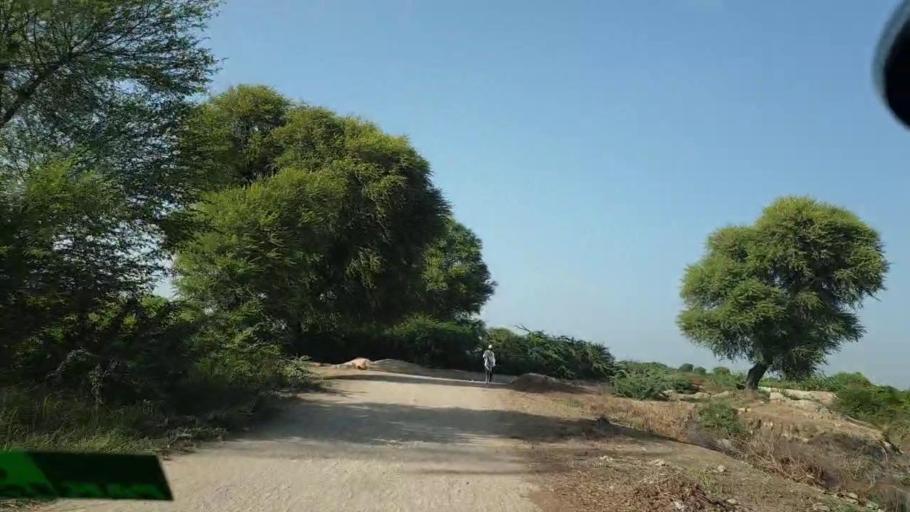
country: PK
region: Sindh
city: Naukot
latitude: 24.7404
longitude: 69.2203
